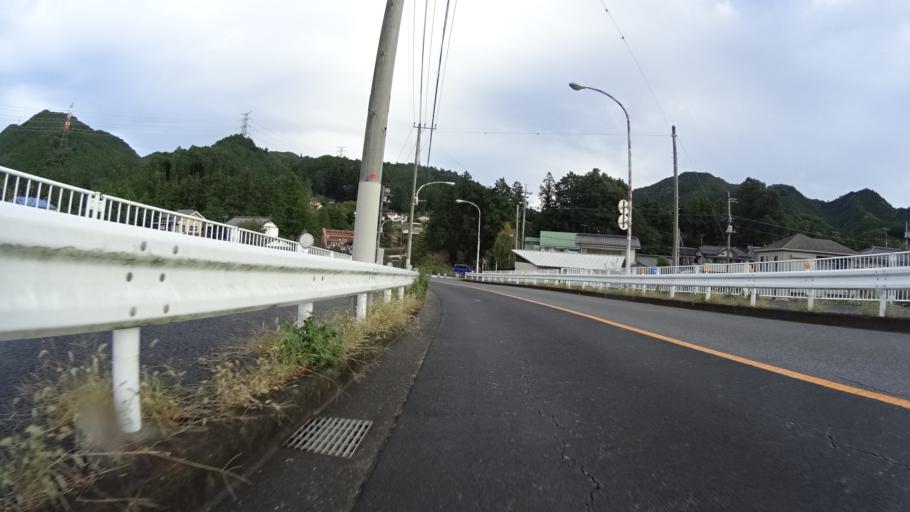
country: JP
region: Tokyo
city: Ome
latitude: 35.8039
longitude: 139.2083
